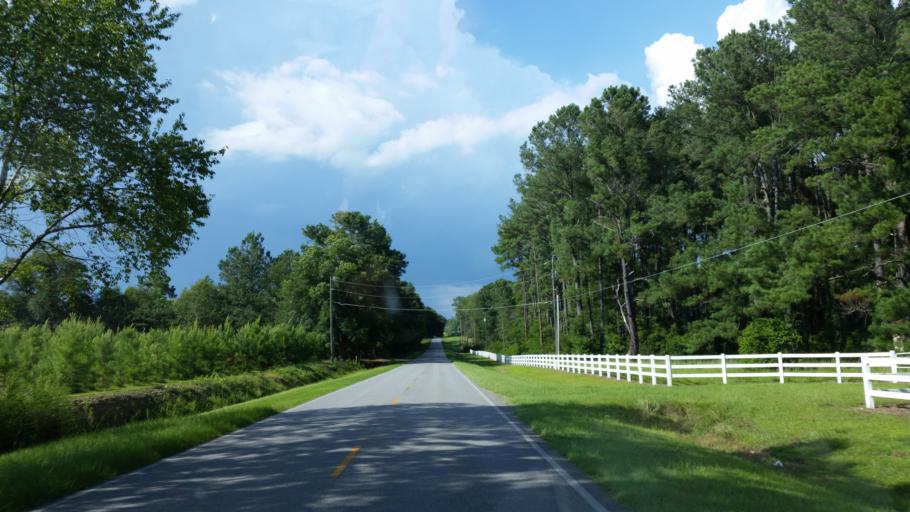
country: US
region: Georgia
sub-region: Lowndes County
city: Hahira
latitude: 30.9630
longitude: -83.4040
